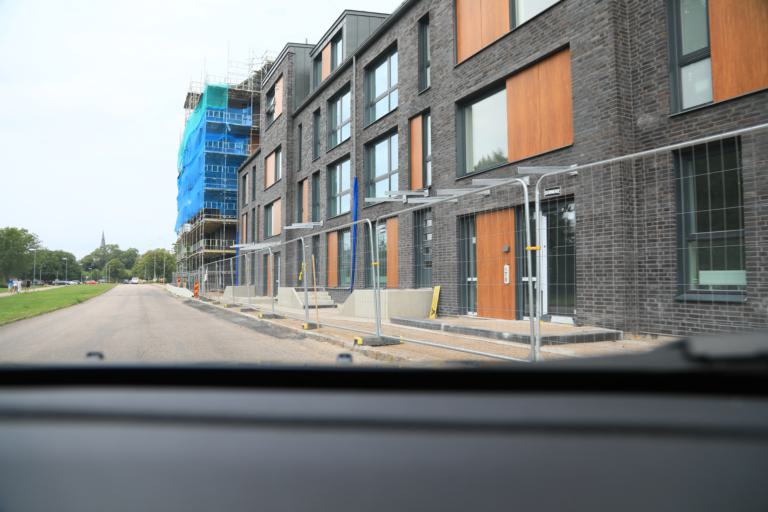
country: SE
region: Halland
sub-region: Halmstads Kommun
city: Halmstad
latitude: 56.6675
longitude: 12.8556
